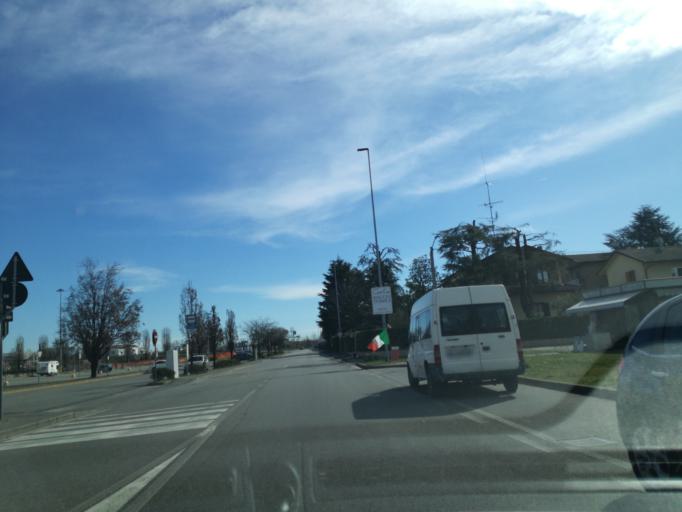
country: IT
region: Lombardy
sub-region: Provincia di Monza e Brianza
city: Villasanta
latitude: 45.6172
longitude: 9.3078
